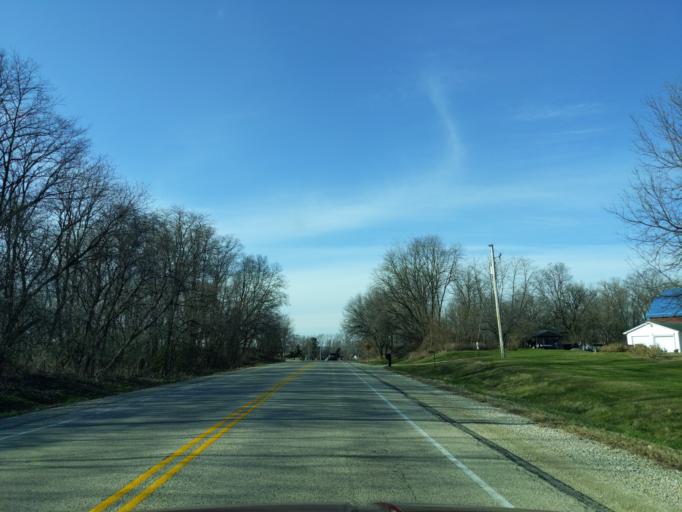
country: US
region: Wisconsin
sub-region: Rock County
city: Milton
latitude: 42.8235
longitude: -88.9579
